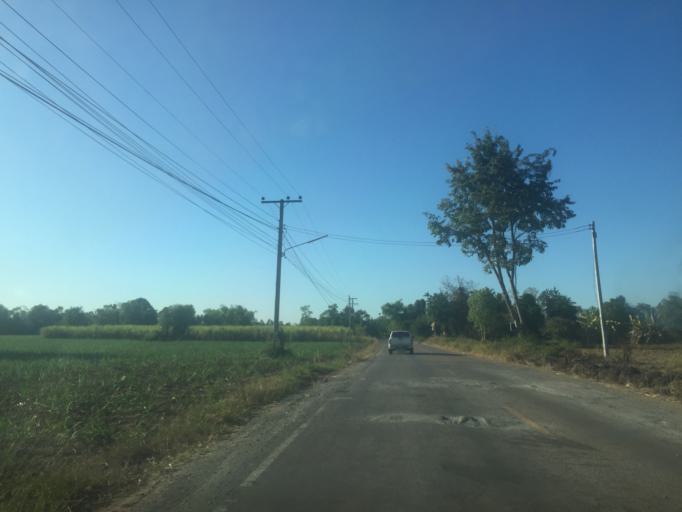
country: TH
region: Kalasin
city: Tha Khantho
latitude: 16.9723
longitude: 103.2646
